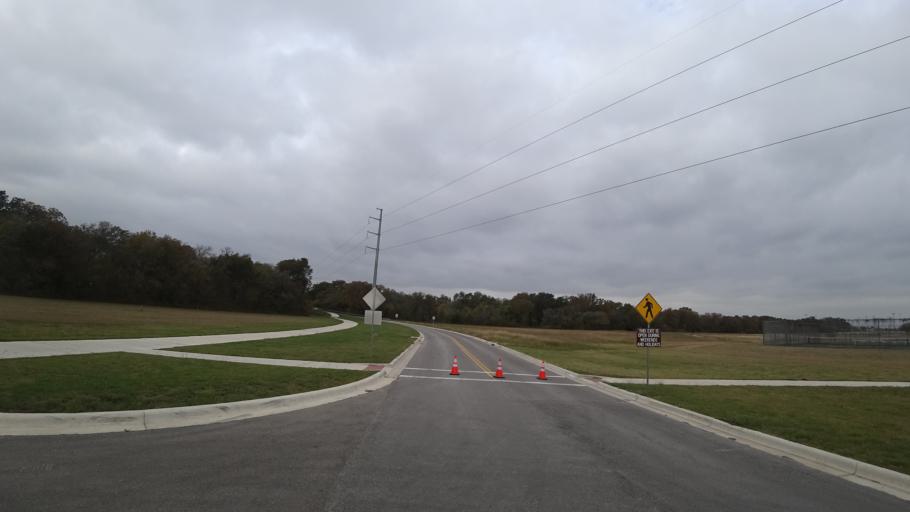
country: US
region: Texas
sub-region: Travis County
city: Pflugerville
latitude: 30.4088
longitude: -97.5988
